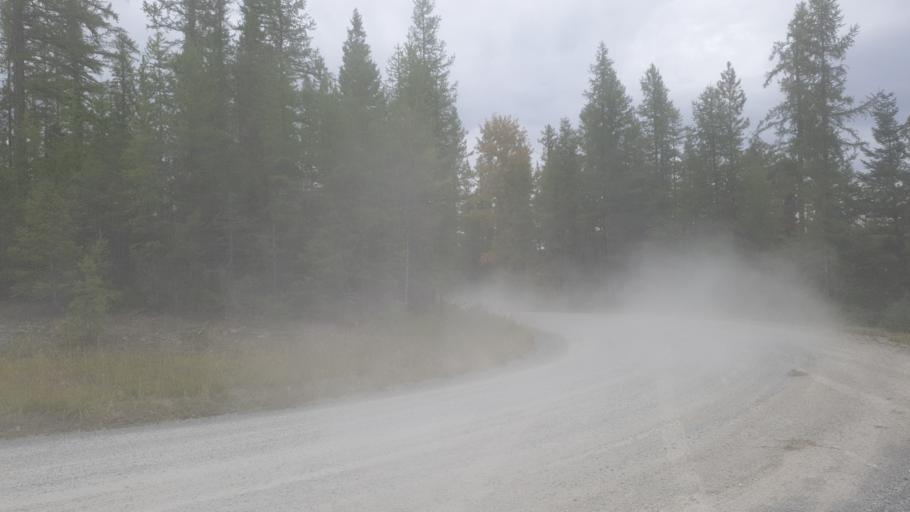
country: US
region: Montana
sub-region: Flathead County
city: Lakeside
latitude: 47.9893
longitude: -114.3233
